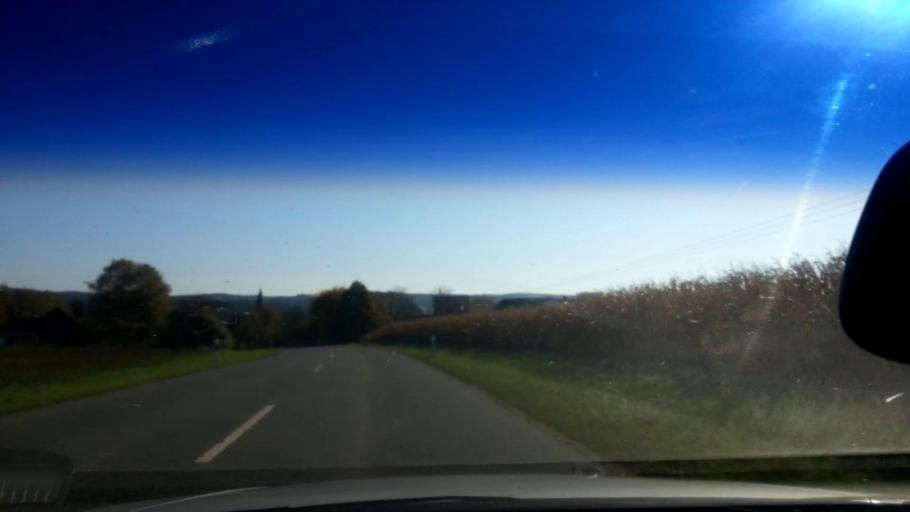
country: DE
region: Bavaria
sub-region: Upper Franconia
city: Wonsees
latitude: 49.9780
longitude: 11.2926
